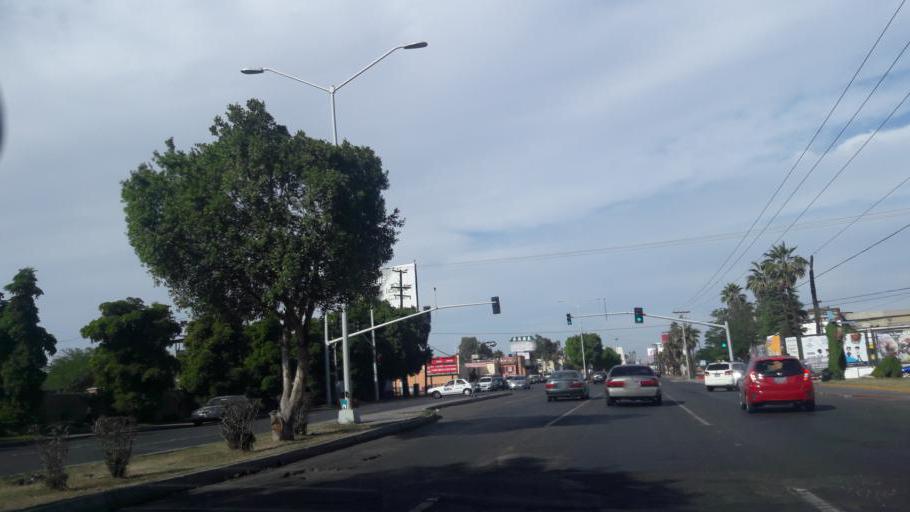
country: MX
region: Baja California
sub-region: Mexicali
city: Mexicali
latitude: 32.6436
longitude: -115.4508
